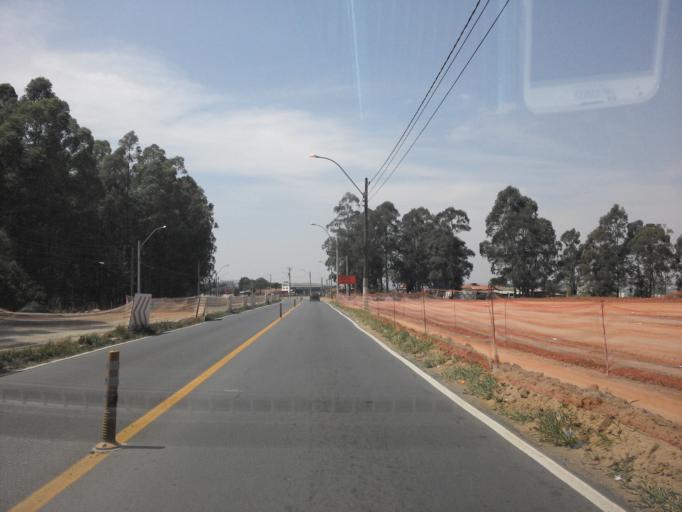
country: BR
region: Sao Paulo
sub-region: Hortolandia
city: Hortolandia
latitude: -22.9427
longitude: -47.1792
